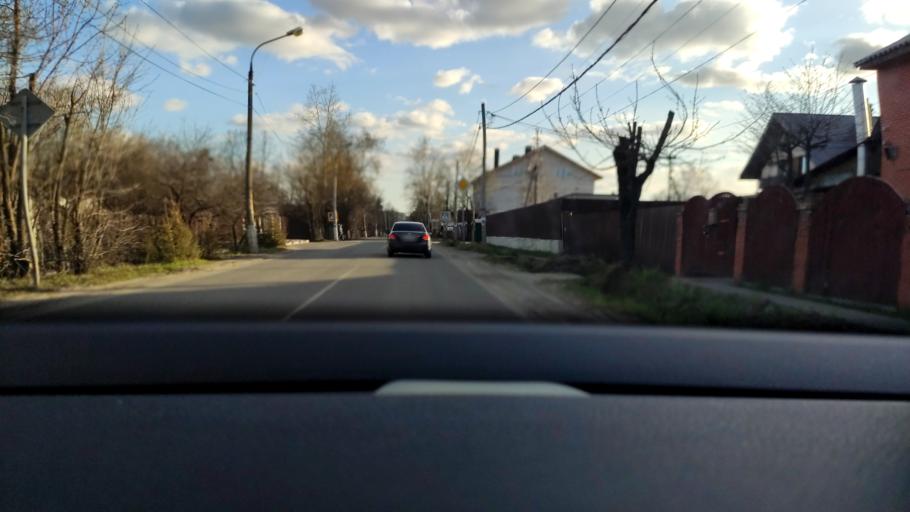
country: RU
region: Moskovskaya
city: Saltykovka
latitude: 55.7734
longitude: 37.8983
